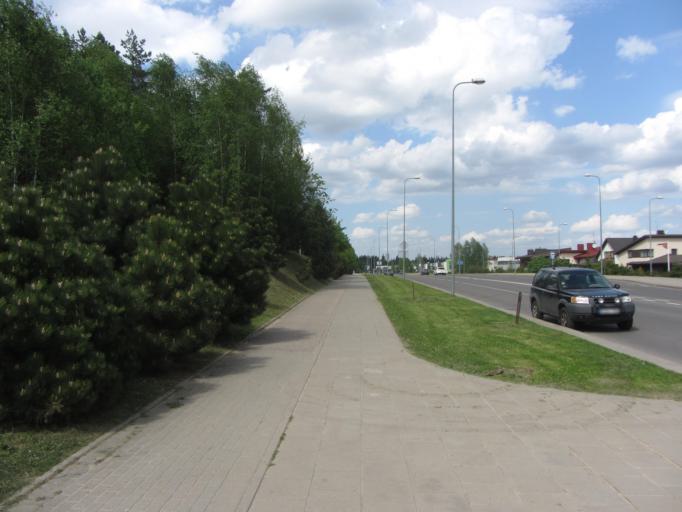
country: LT
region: Vilnius County
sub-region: Vilnius
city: Fabijoniskes
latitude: 54.7585
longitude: 25.2810
